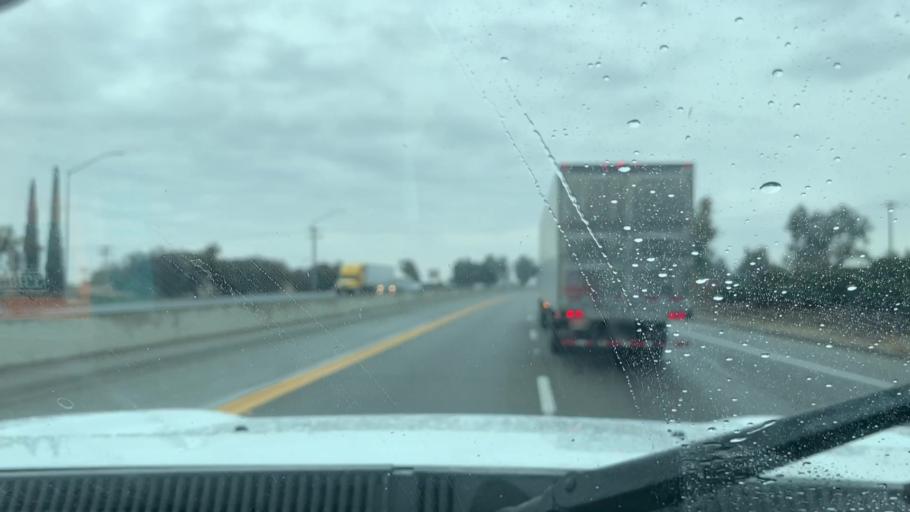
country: US
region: California
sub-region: Kern County
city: Delano
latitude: 35.7785
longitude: -119.2529
